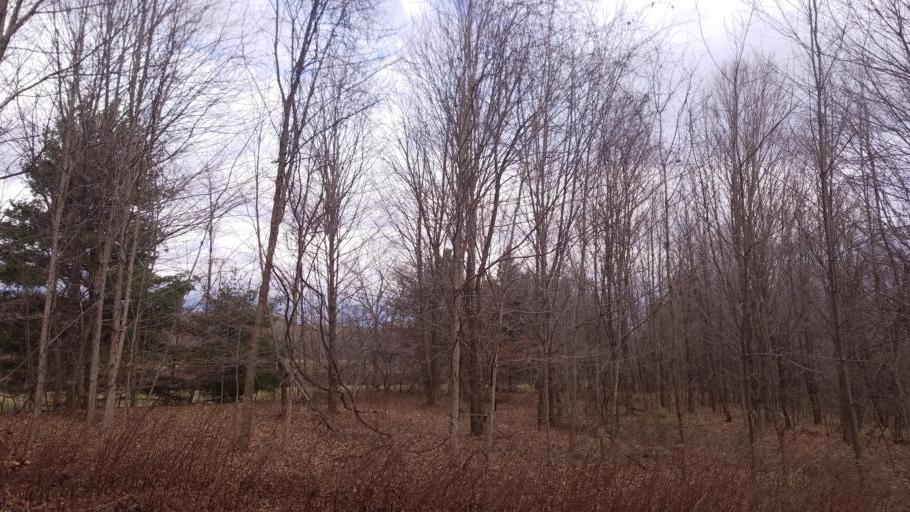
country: US
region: Ohio
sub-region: Knox County
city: Mount Vernon
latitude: 40.3347
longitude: -82.5646
